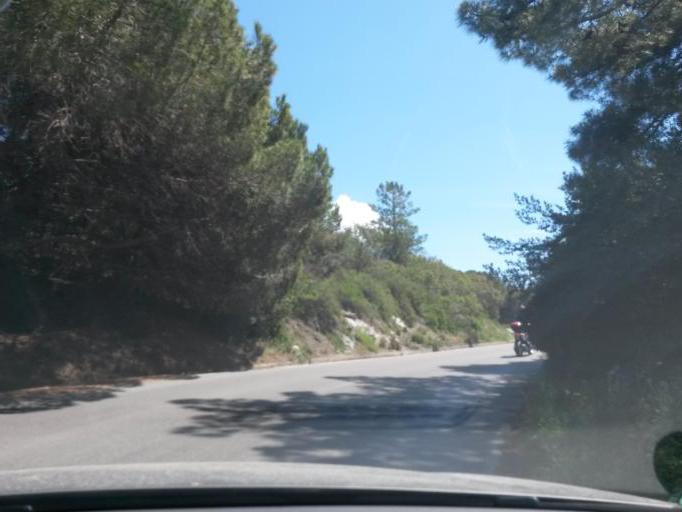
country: IT
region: Tuscany
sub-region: Provincia di Livorno
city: Portoferraio
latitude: 42.7655
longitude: 10.3242
